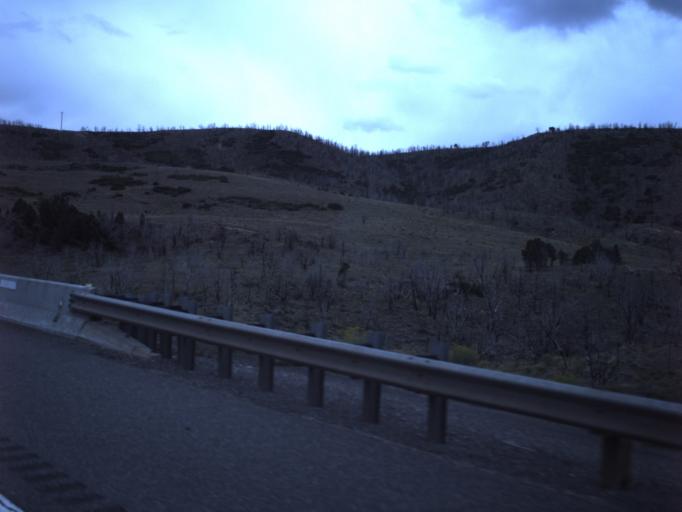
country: US
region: Utah
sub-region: Sevier County
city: Monroe
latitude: 38.5552
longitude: -112.4238
